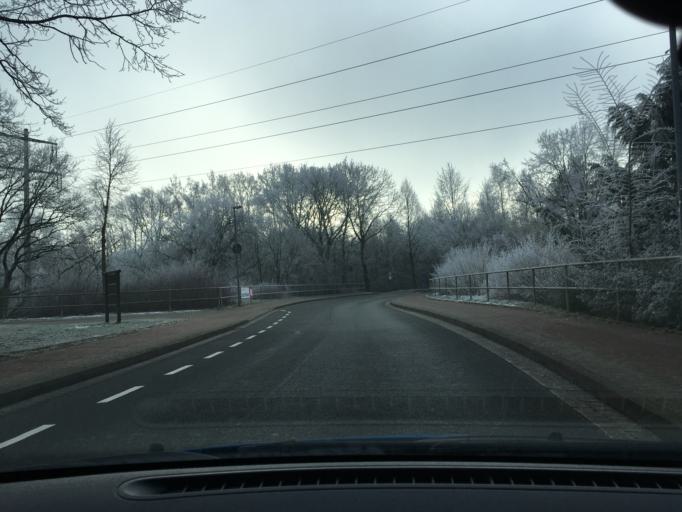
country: DE
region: Lower Saxony
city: Bardowick
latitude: 53.2729
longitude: 10.3890
